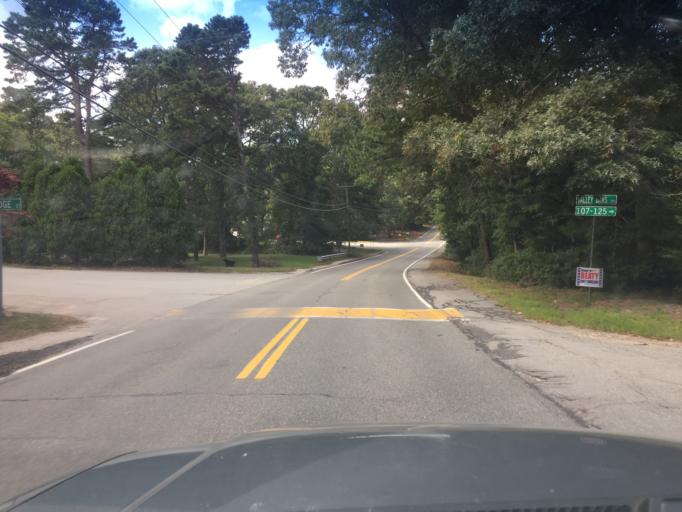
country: US
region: Massachusetts
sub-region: Barnstable County
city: Monument Beach
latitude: 41.7155
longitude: -70.5930
